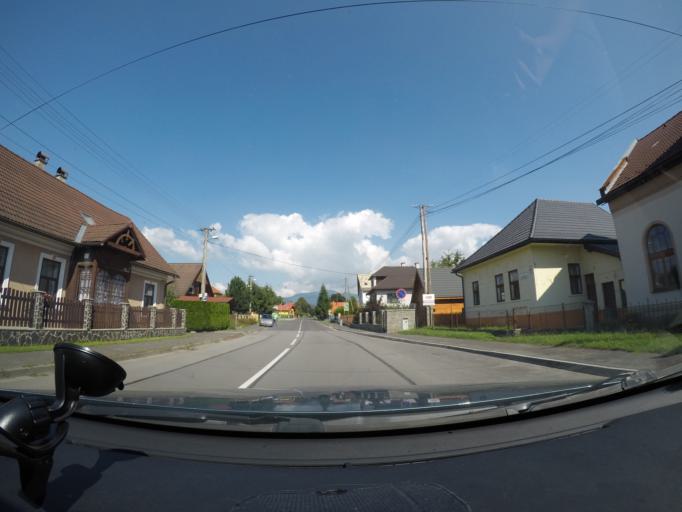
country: SK
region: Zilinsky
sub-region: Okres Liptovsky Mikulas
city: Liptovsky Mikulas
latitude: 49.0977
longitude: 19.5897
